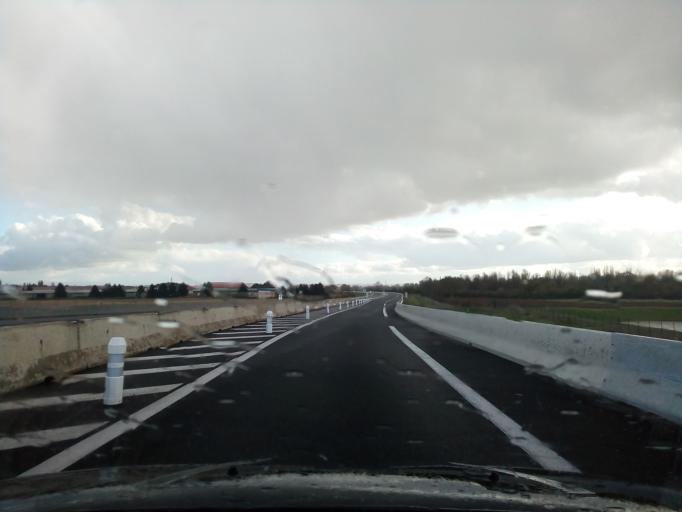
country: FR
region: Auvergne
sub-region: Departement de l'Allier
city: Varennes-sur-Allier
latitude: 46.3225
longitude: 3.3802
